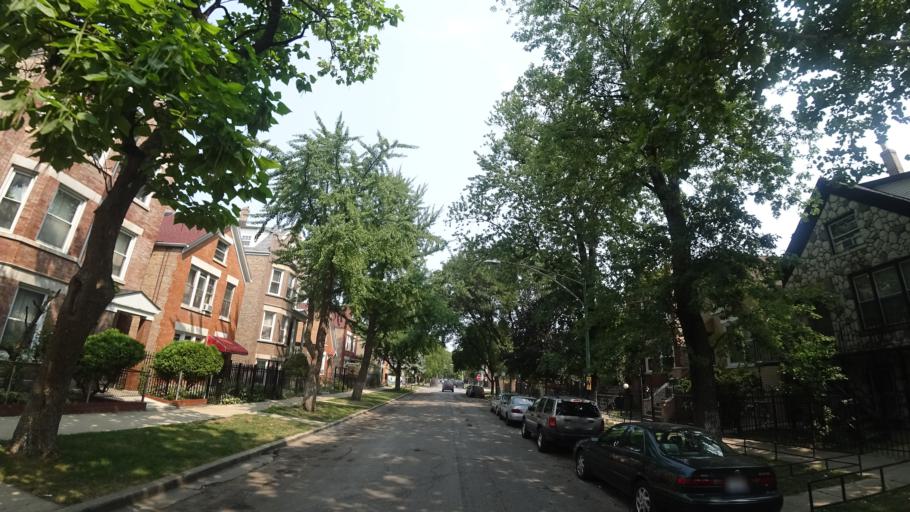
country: US
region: Illinois
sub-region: Cook County
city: Cicero
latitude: 41.8417
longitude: -87.7208
